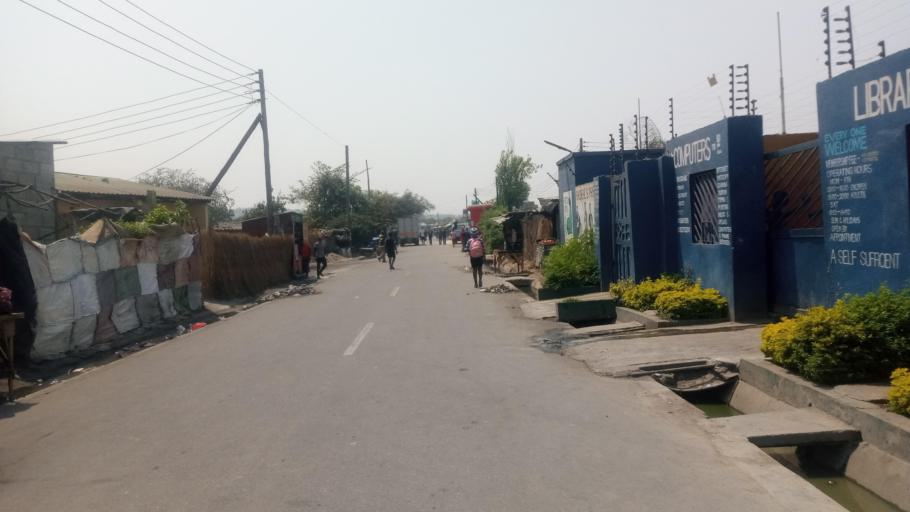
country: ZM
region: Lusaka
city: Lusaka
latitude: -15.4447
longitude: 28.3779
